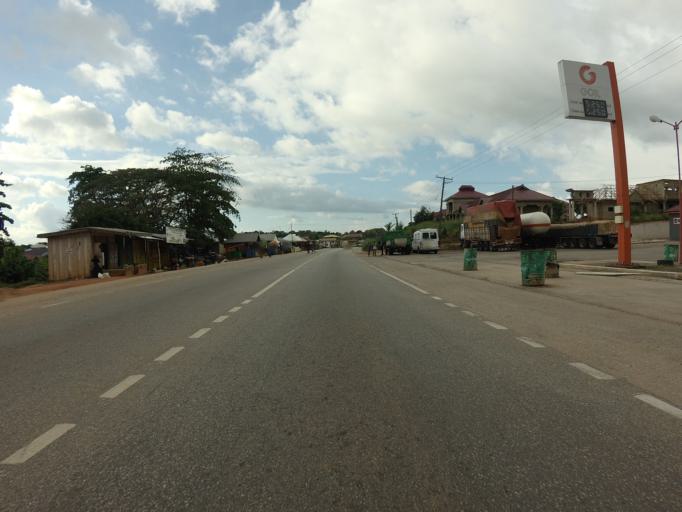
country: GH
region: Ashanti
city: Tafo
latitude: 6.8398
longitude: -1.6503
